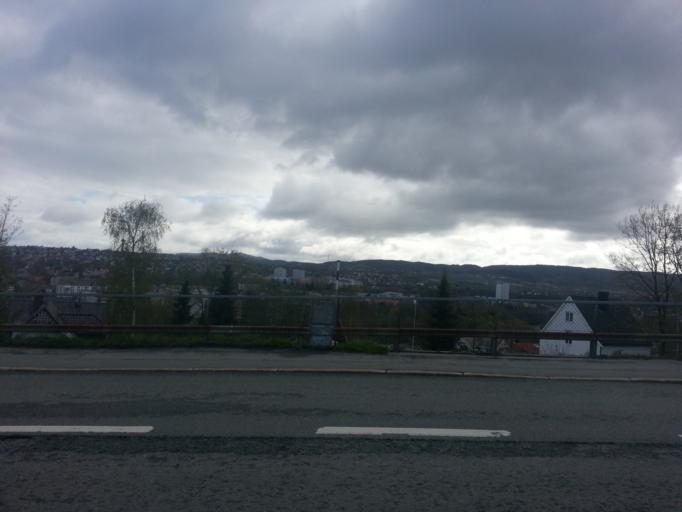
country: NO
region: Sor-Trondelag
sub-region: Trondheim
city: Trondheim
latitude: 63.4203
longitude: 10.3731
